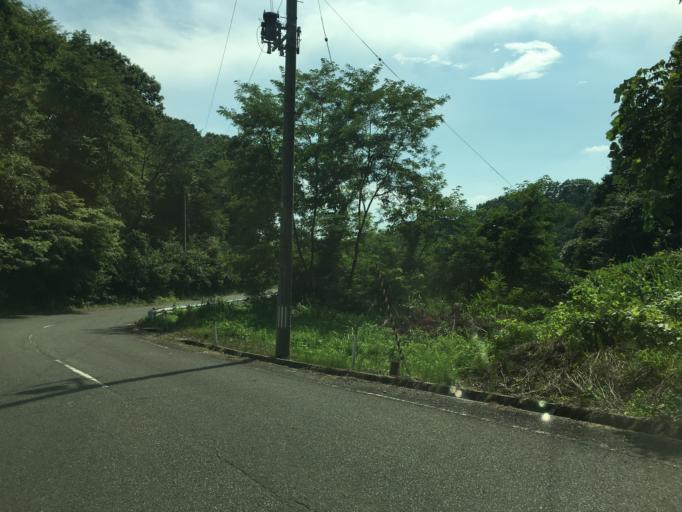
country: JP
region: Fukushima
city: Sukagawa
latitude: 37.2294
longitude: 140.4218
